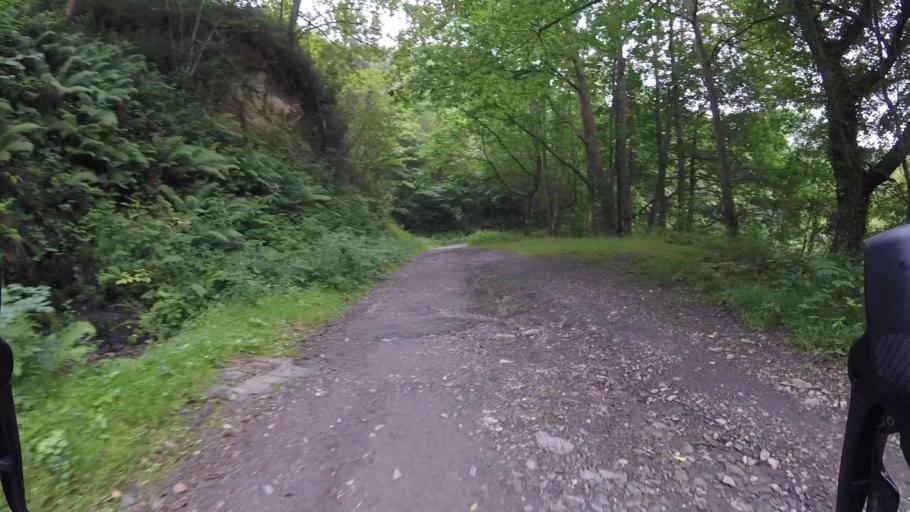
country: ES
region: Navarre
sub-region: Provincia de Navarra
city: Arano
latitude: 43.2551
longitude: -1.8873
